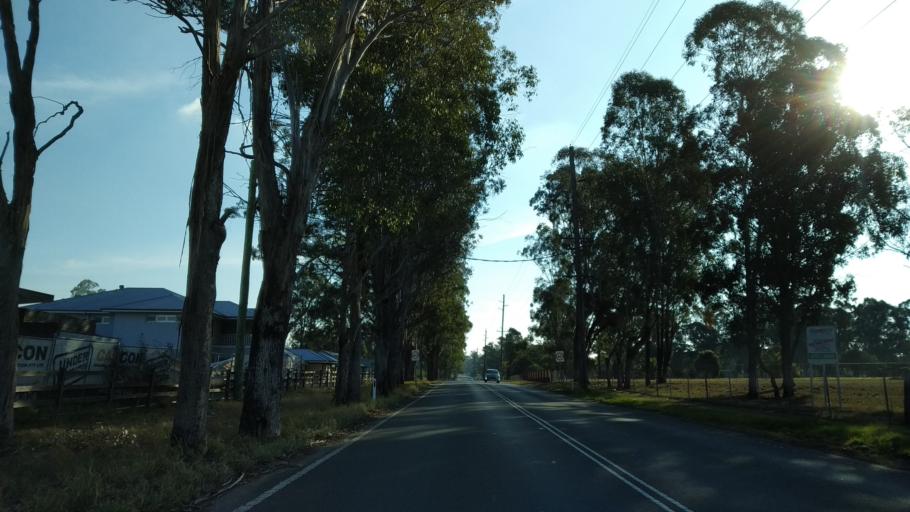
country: AU
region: New South Wales
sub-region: Penrith Municipality
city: Werrington Downs
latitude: -33.7141
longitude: 150.7392
